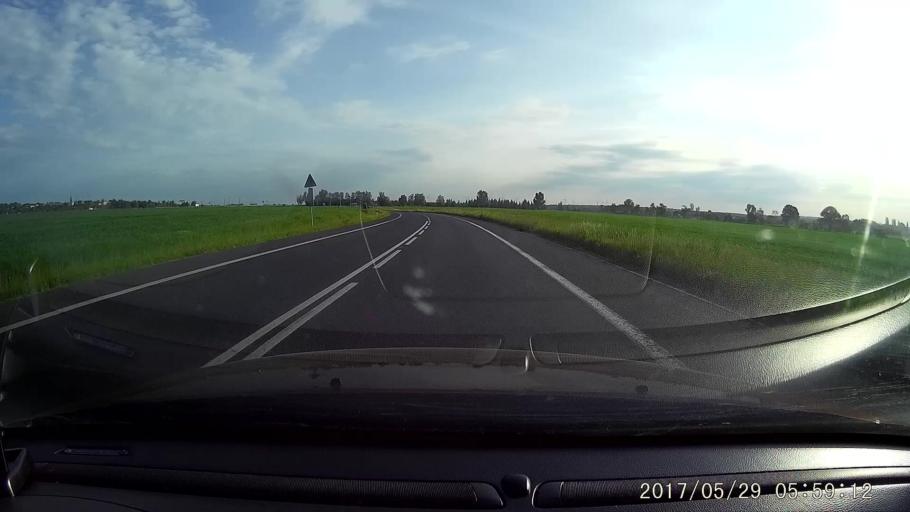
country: PL
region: Lower Silesian Voivodeship
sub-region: Powiat zgorzelecki
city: Lagow
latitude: 51.1406
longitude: 15.0337
